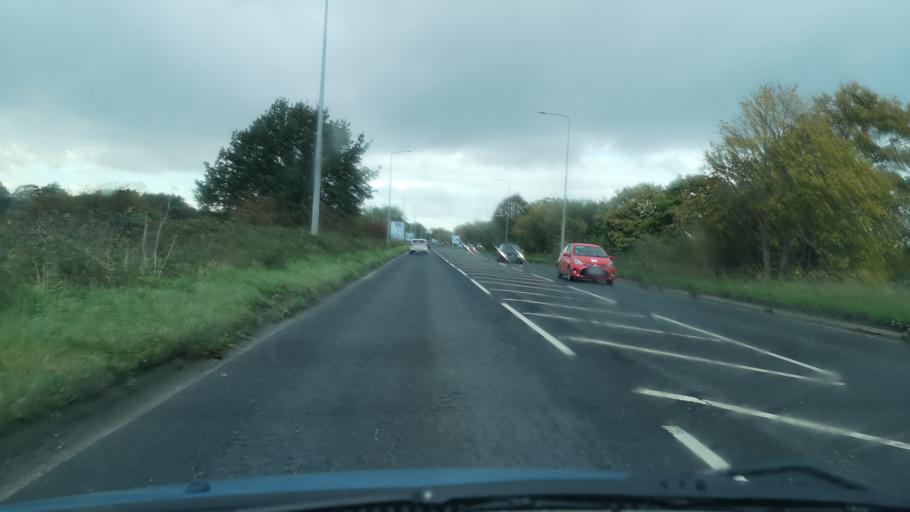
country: GB
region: England
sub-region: North Lincolnshire
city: Crowle
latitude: 53.5839
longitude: -0.8130
